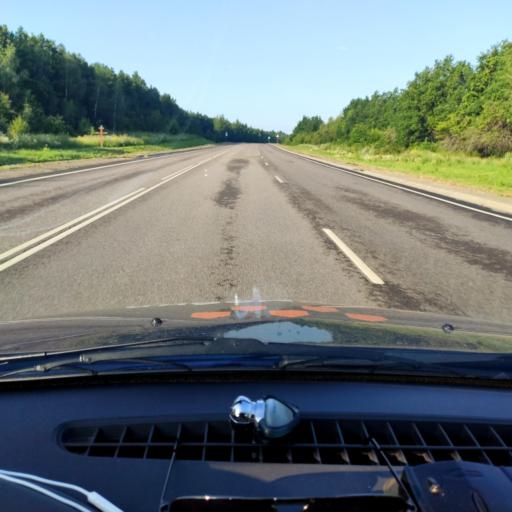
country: RU
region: Lipetsk
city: Izmalkovo
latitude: 52.4602
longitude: 38.0115
